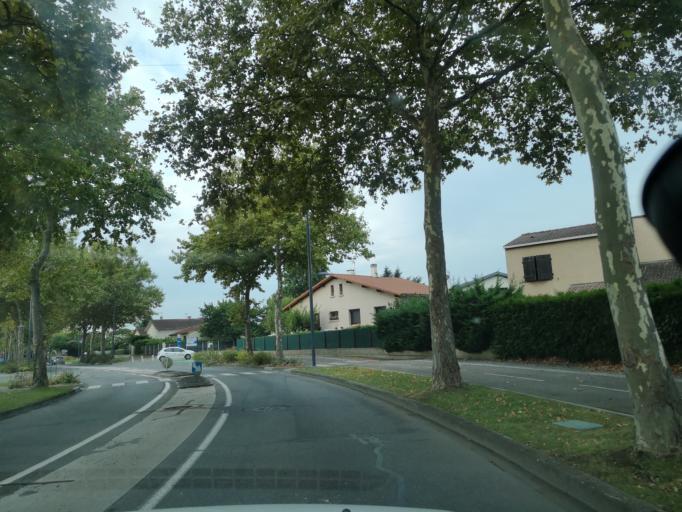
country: FR
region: Midi-Pyrenees
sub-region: Departement de la Haute-Garonne
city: Blagnac
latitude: 43.6302
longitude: 1.3876
